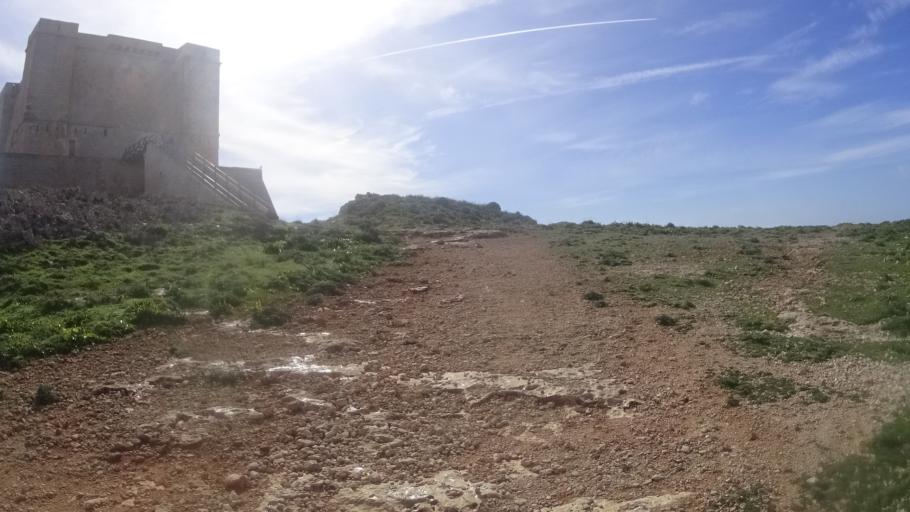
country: MT
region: Il-Qala
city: Qala
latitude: 36.0073
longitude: 14.3294
